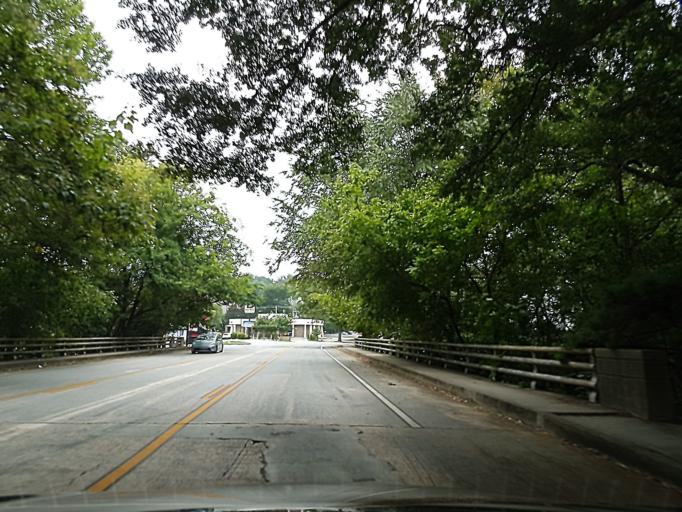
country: US
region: Georgia
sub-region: DeKalb County
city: North Druid Hills
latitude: 33.8352
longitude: -84.3351
